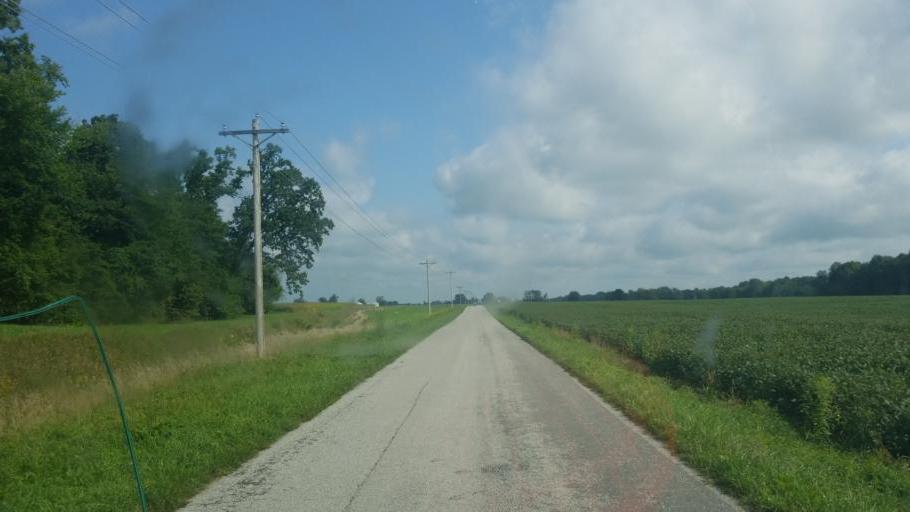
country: US
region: Ohio
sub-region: Marion County
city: Marion
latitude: 40.6052
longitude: -82.9912
